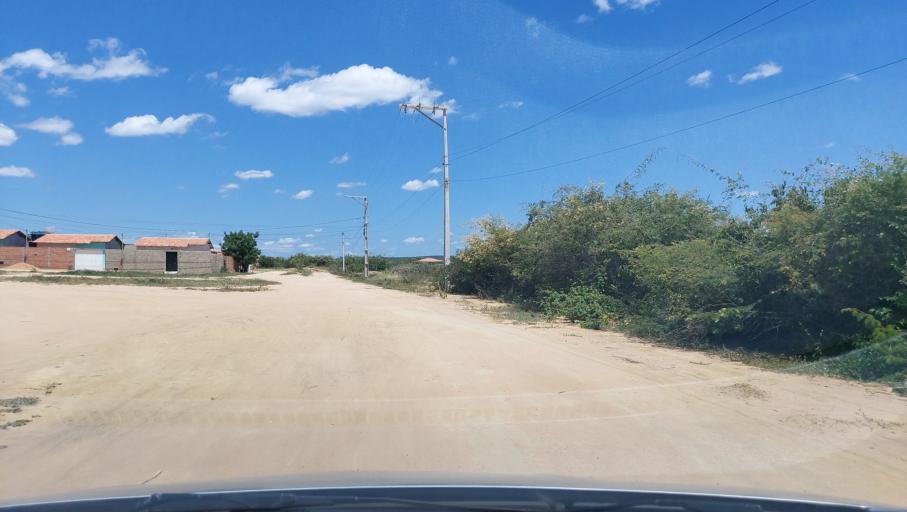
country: BR
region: Bahia
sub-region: Oliveira Dos Brejinhos
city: Beira Rio
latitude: -12.0042
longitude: -42.6328
